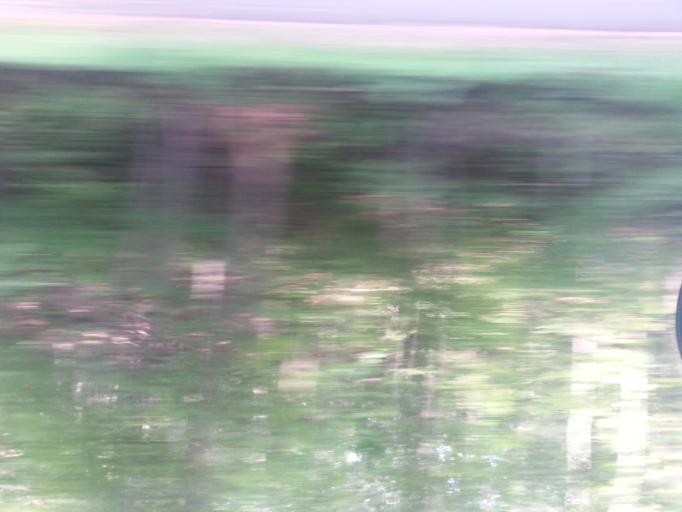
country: US
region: Tennessee
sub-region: Anderson County
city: Oak Ridge
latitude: 35.9312
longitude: -84.3392
